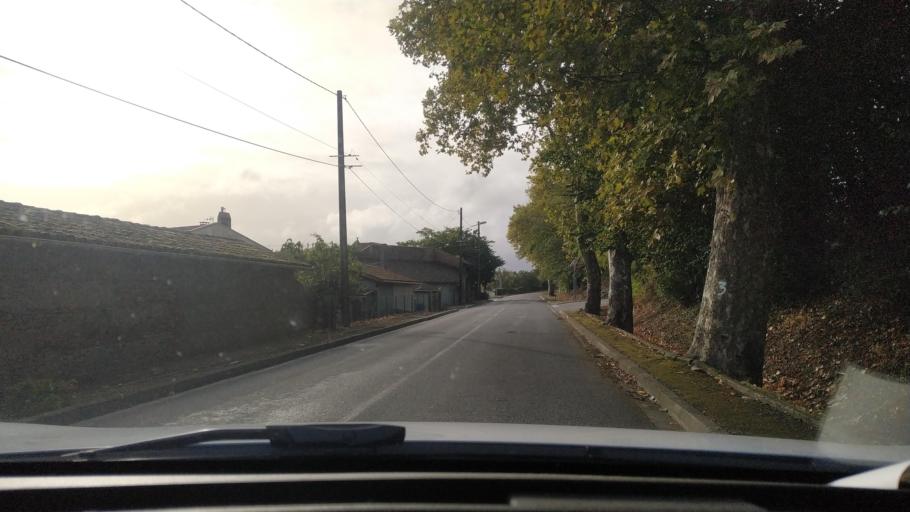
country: FR
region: Midi-Pyrenees
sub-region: Departement de la Haute-Garonne
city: Gaillac-Toulza
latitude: 43.3013
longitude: 1.4691
